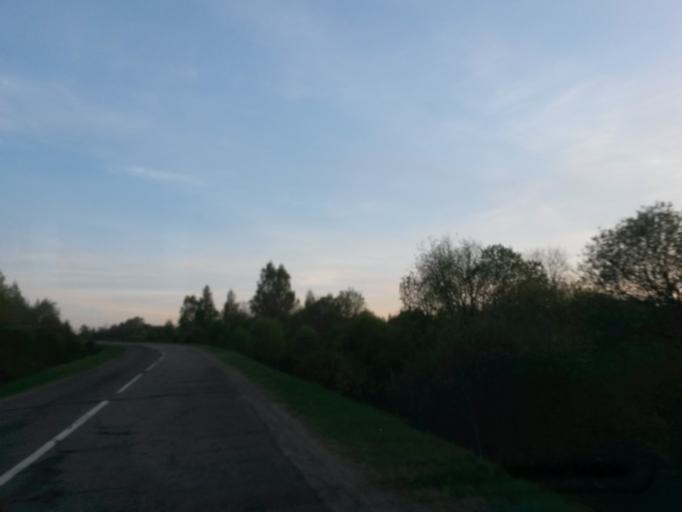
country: RU
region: Jaroslavl
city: Tutayev
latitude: 57.9020
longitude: 39.5749
